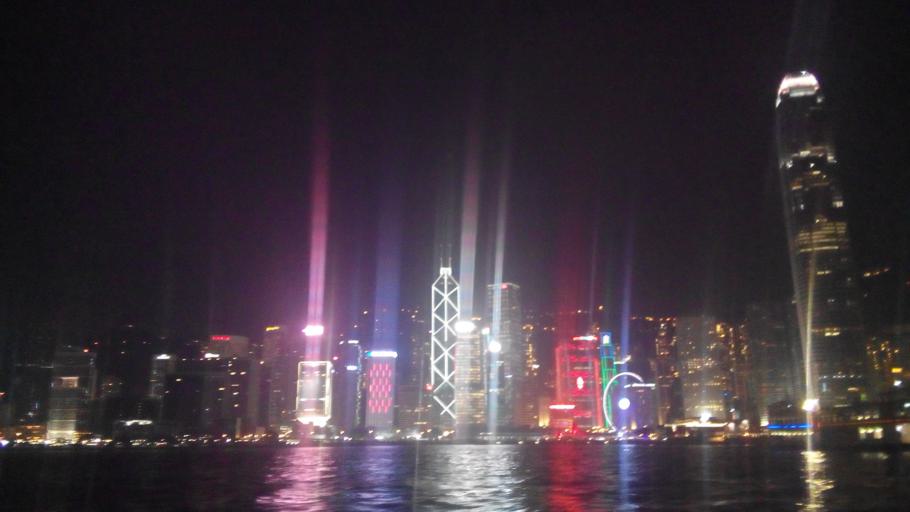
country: HK
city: Hong Kong
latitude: 22.2910
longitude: 114.1653
